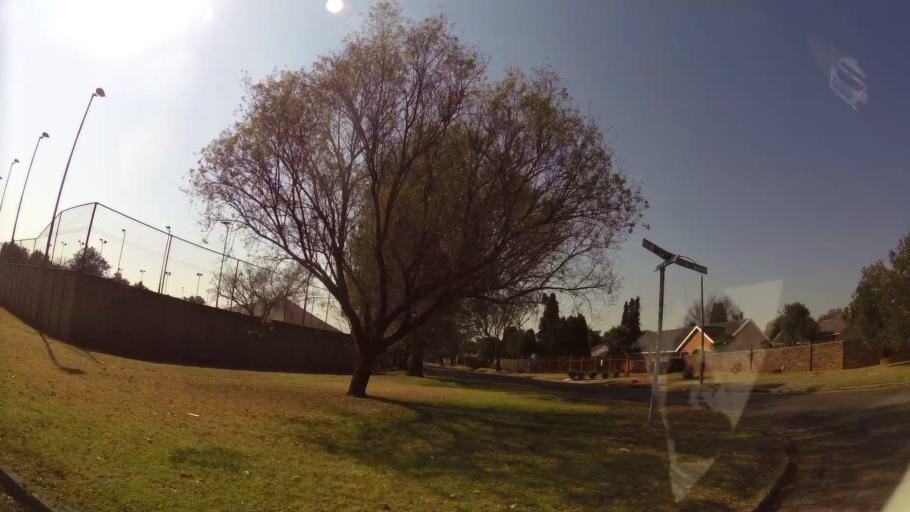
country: ZA
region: Gauteng
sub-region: Ekurhuleni Metropolitan Municipality
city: Boksburg
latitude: -26.2463
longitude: 28.2649
